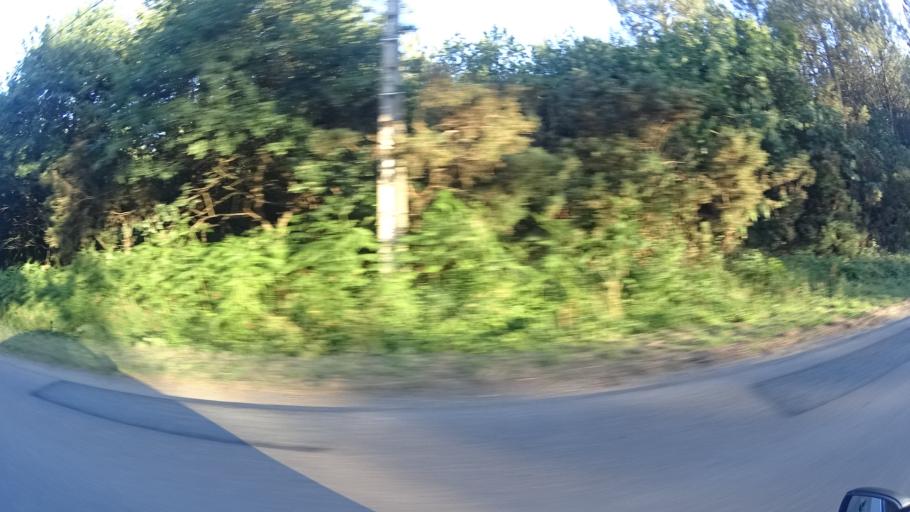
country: FR
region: Brittany
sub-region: Departement d'Ille-et-Vilaine
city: Langon
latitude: 47.7186
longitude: -1.8680
